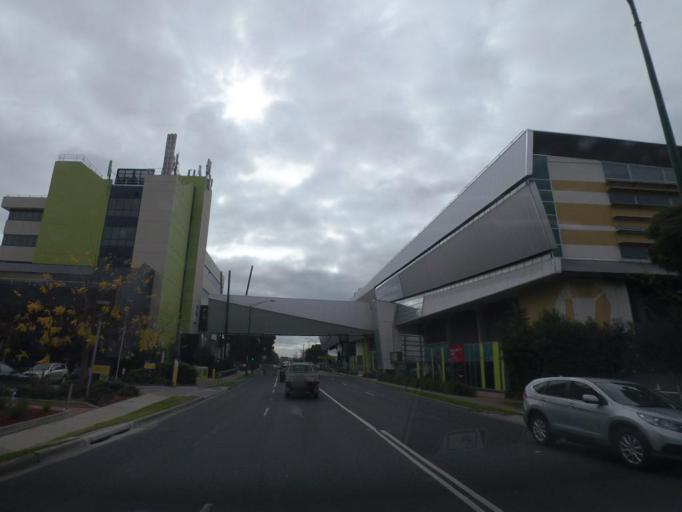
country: AU
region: Victoria
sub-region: Whitehorse
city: Box Hill
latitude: -37.8161
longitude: 145.1151
